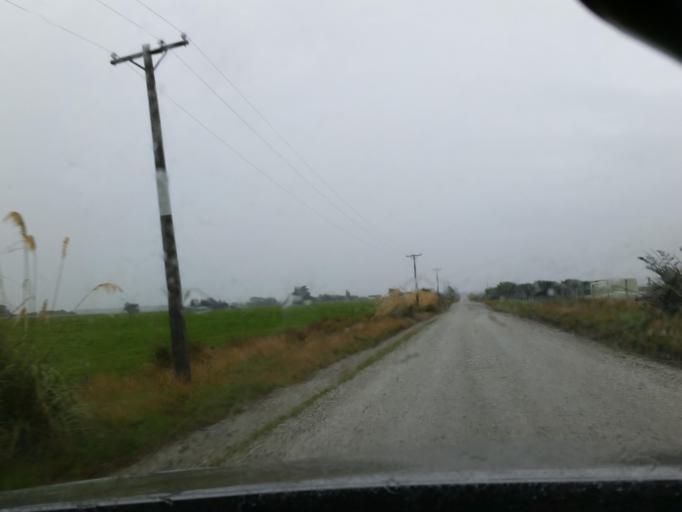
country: NZ
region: Southland
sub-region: Invercargill City
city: Invercargill
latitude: -46.4424
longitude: 168.5062
